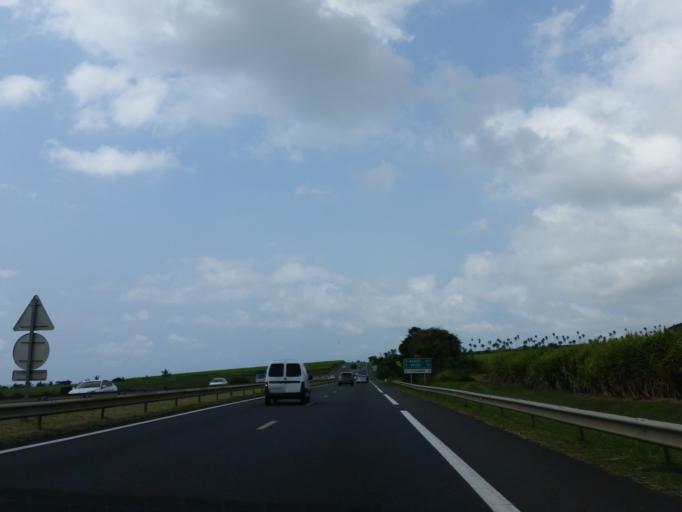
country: RE
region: Reunion
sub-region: Reunion
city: Sainte-Suzanne
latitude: -20.8993
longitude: 55.5810
